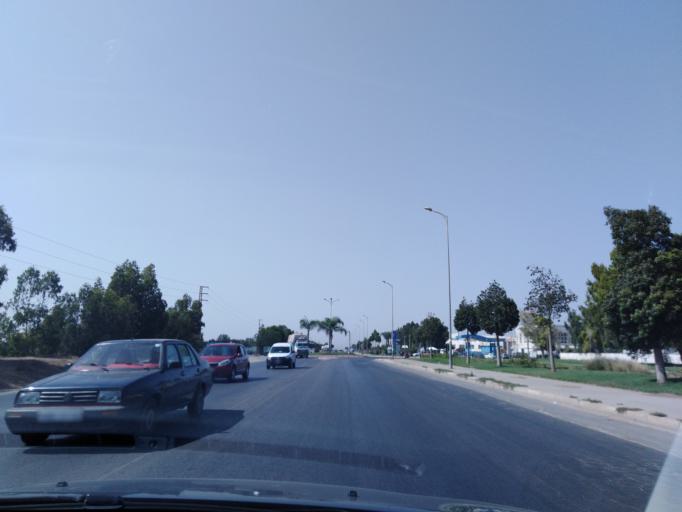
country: MA
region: Chaouia-Ouardigha
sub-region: Settat Province
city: Berrechid
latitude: 33.2534
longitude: -7.5837
